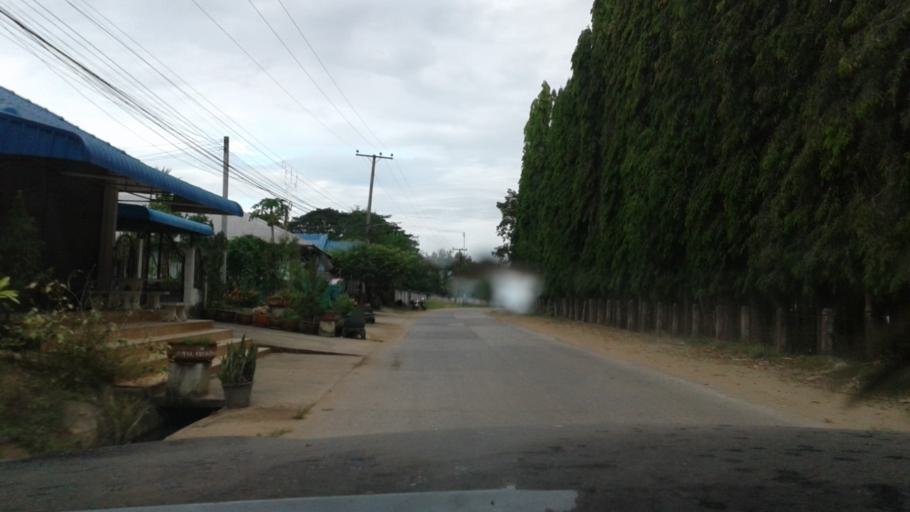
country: TH
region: Changwat Udon Thani
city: Nong Wua So
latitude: 17.2413
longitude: 102.5353
